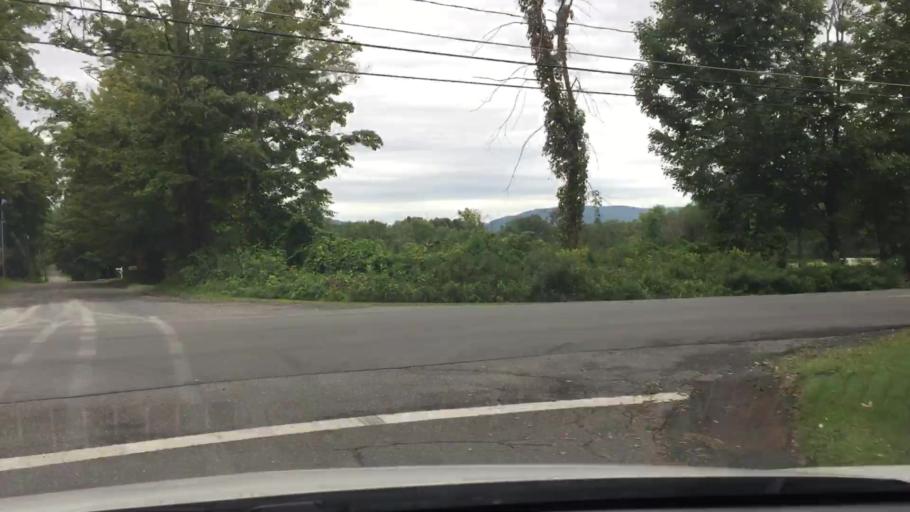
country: US
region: Massachusetts
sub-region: Berkshire County
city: Richmond
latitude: 42.3958
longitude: -73.3541
